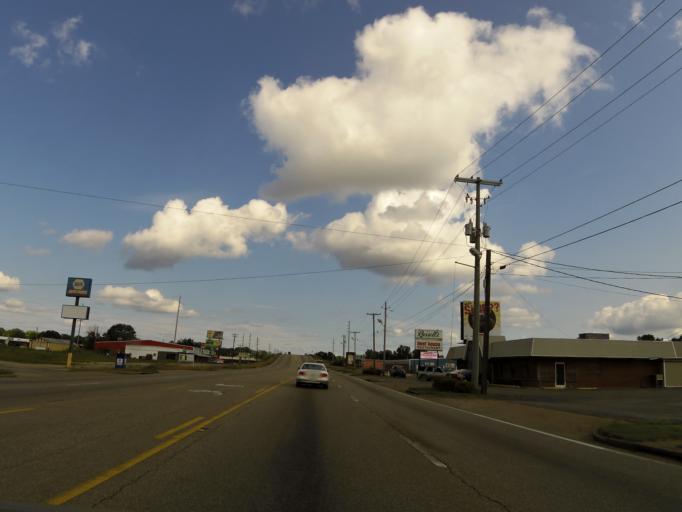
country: US
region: Mississippi
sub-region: Alcorn County
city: Corinth
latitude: 34.9249
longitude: -88.5227
